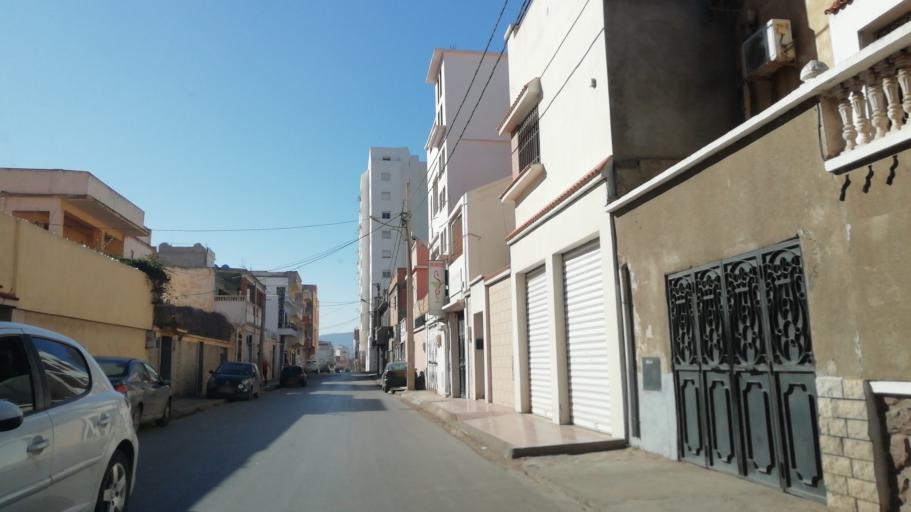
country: DZ
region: Oran
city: Oran
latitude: 35.7045
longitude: -0.6087
